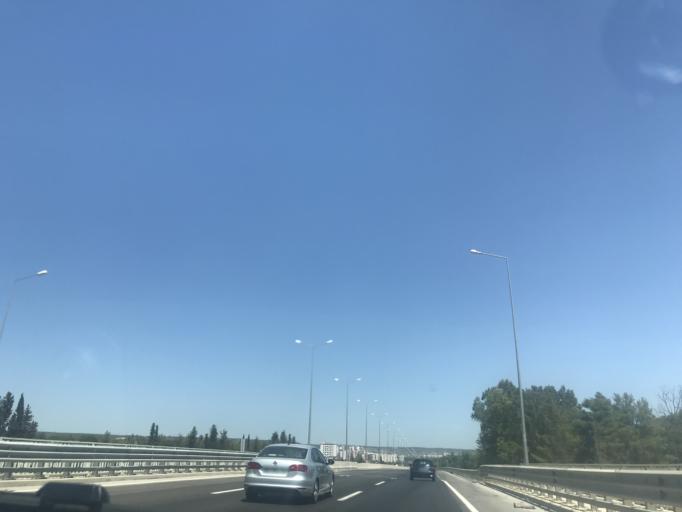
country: TR
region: Antalya
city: Cakirlar
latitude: 36.8873
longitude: 30.6119
